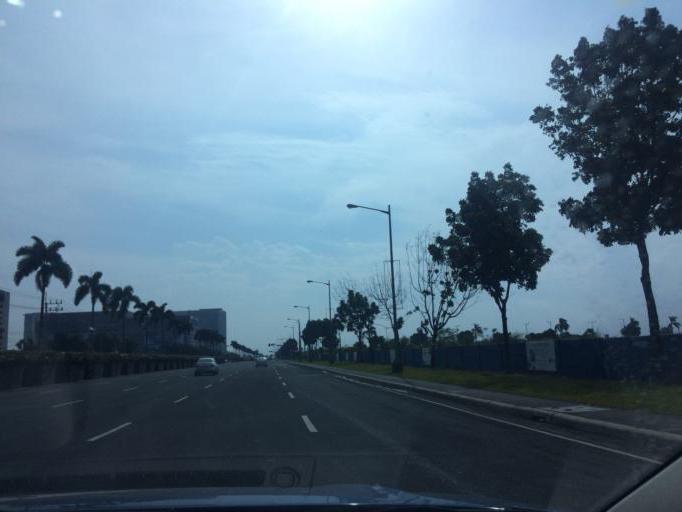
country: PH
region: Metro Manila
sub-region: Makati City
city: Makati City
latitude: 14.5249
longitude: 120.9875
